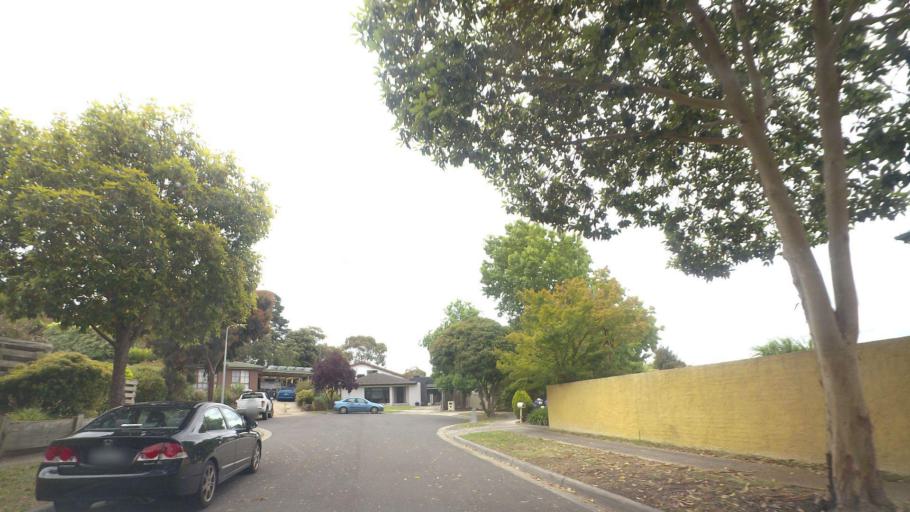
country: AU
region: Victoria
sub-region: Knox
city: Wantirna
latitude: -37.8562
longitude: 145.2372
